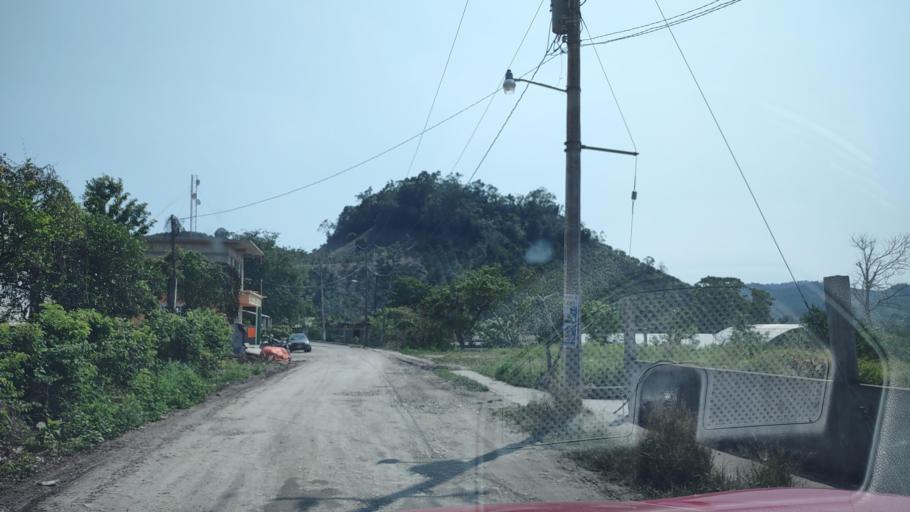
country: MX
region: Veracruz
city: Agua Dulce
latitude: 20.3176
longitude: -97.1759
